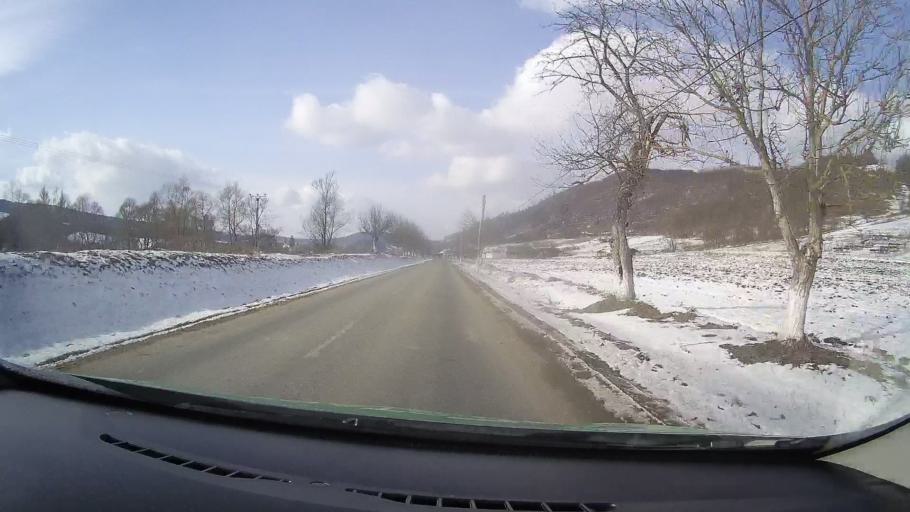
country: RO
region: Sibiu
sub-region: Comuna Iacobeni
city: Iacobeni
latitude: 46.0424
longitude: 24.7292
